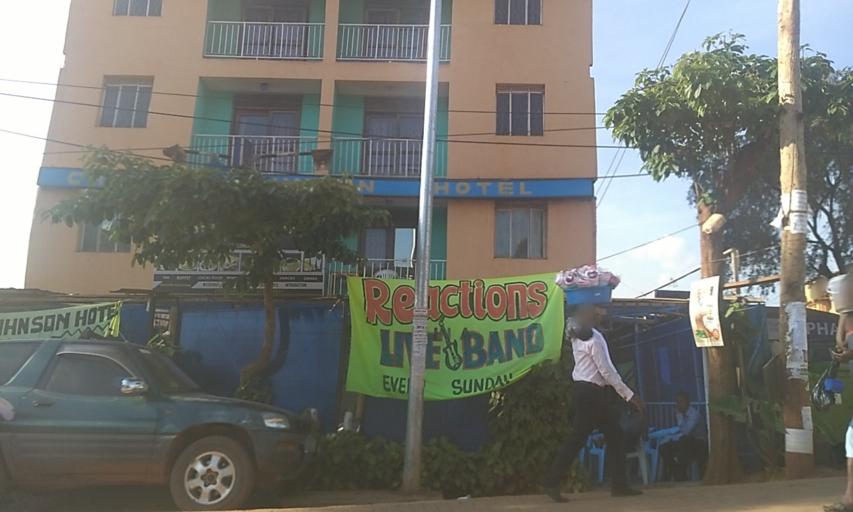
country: UG
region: Central Region
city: Kampala Central Division
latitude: 0.3276
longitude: 32.5645
